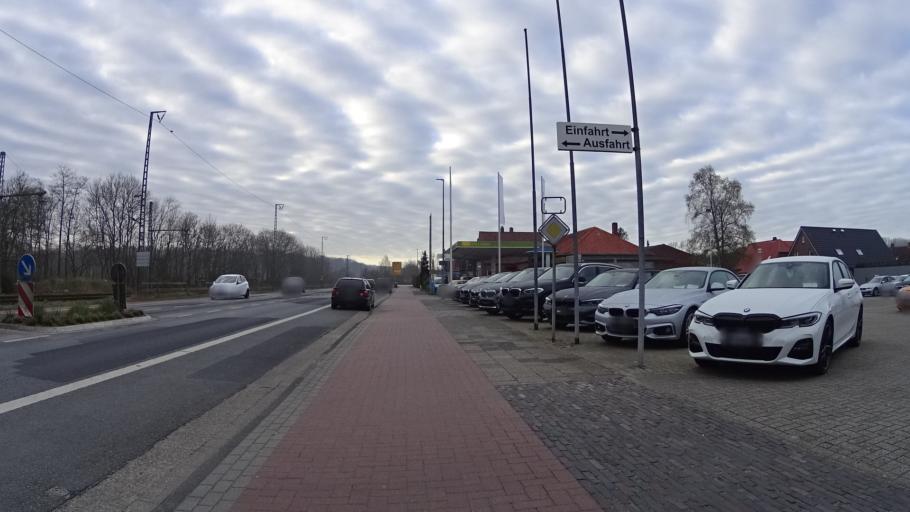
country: DE
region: Lower Saxony
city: Norden
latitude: 53.5848
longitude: 7.2236
